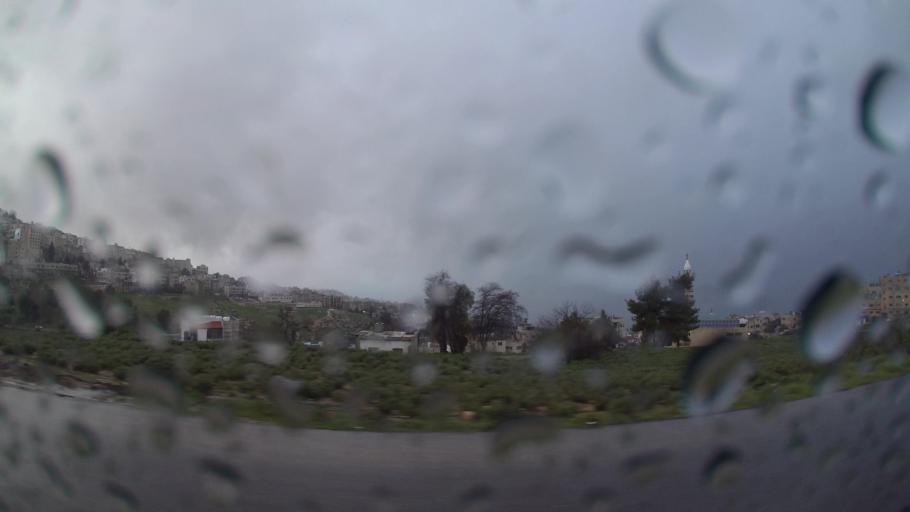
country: JO
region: Amman
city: Al Jubayhah
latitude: 32.0297
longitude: 35.8428
